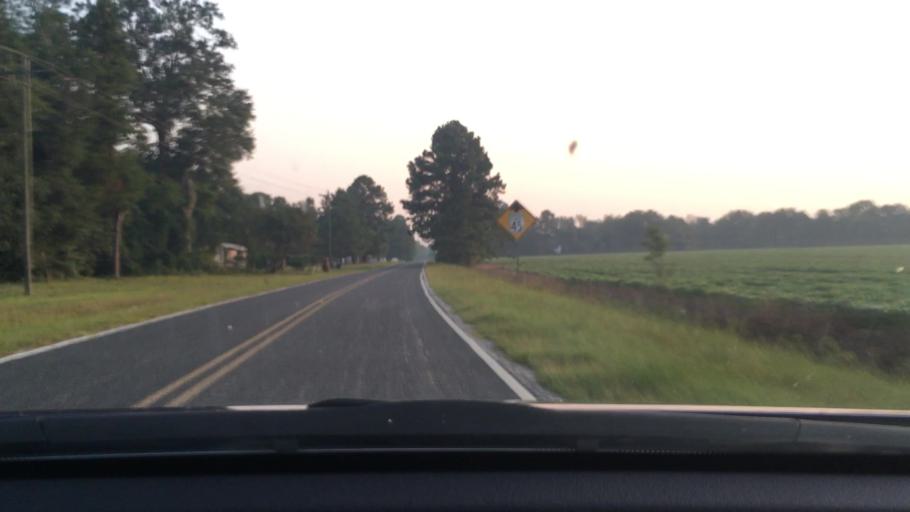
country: US
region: South Carolina
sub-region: Lee County
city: Bishopville
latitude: 34.2306
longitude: -80.1332
